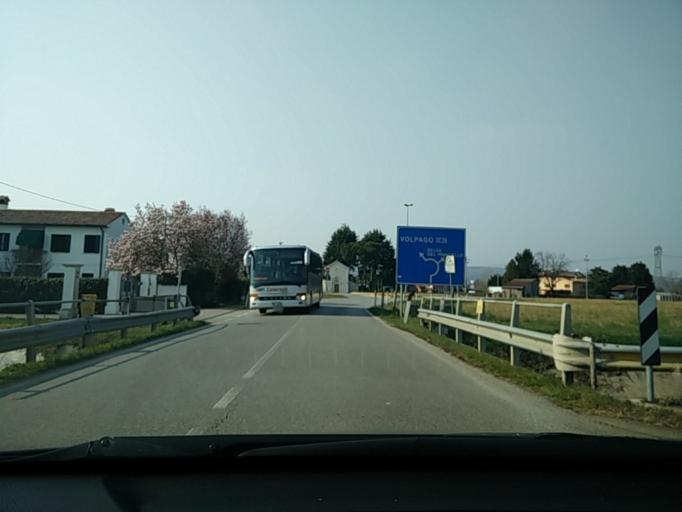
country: IT
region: Veneto
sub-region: Provincia di Treviso
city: Camalo
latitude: 45.7622
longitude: 12.1576
